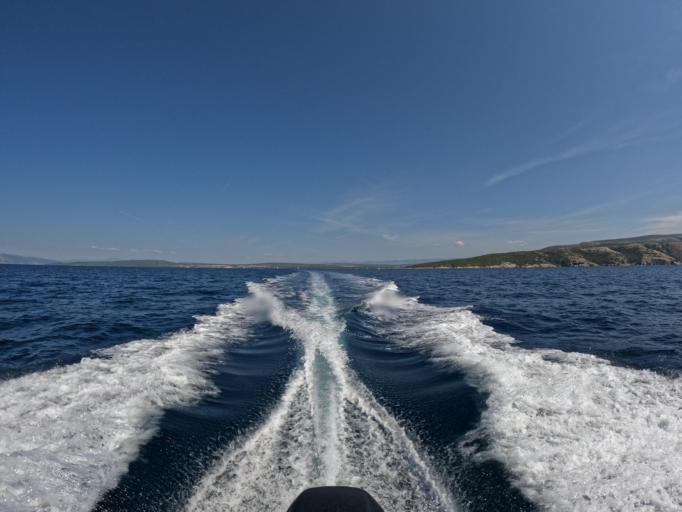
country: HR
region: Primorsko-Goranska
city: Punat
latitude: 44.9632
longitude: 14.6094
